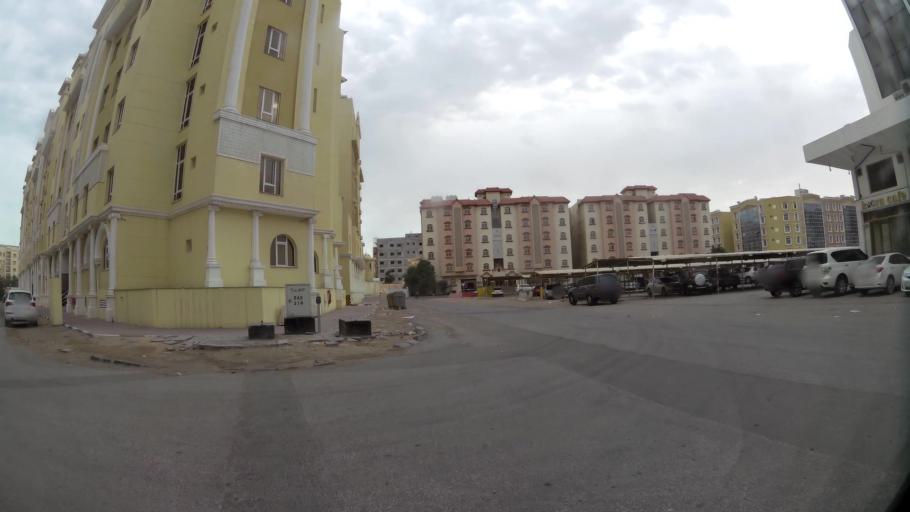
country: QA
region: Baladiyat ad Dawhah
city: Doha
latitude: 25.2801
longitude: 51.5006
